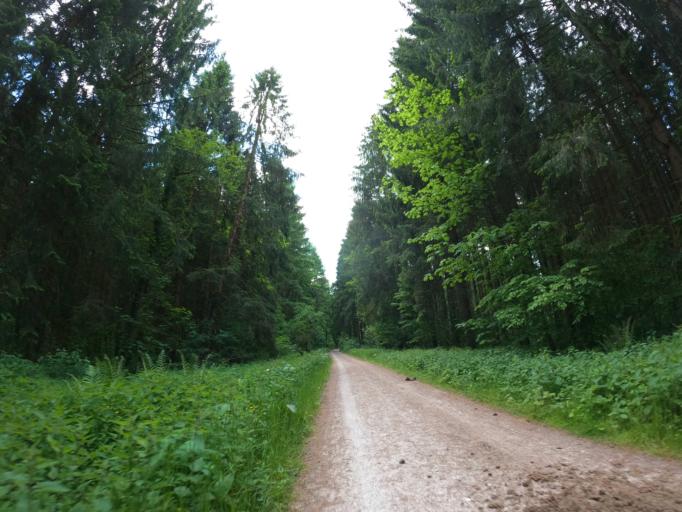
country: DE
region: Bavaria
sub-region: Upper Bavaria
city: Sauerlach
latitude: 47.9929
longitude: 11.6387
